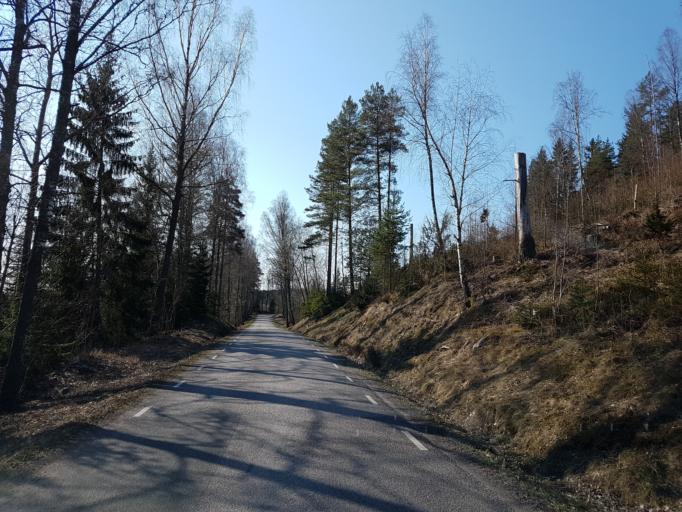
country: SE
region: Kalmar
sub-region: Vasterviks Kommun
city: Overum
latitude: 58.1804
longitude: 16.2806
